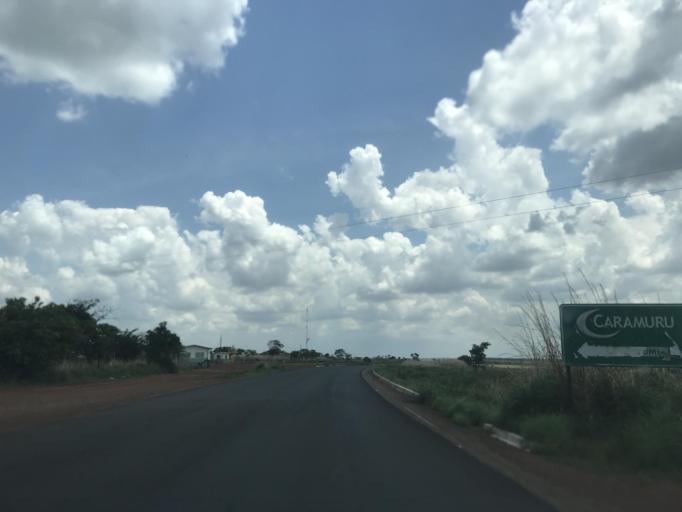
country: BR
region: Goias
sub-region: Piracanjuba
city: Piracanjuba
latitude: -17.3422
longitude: -48.7928
